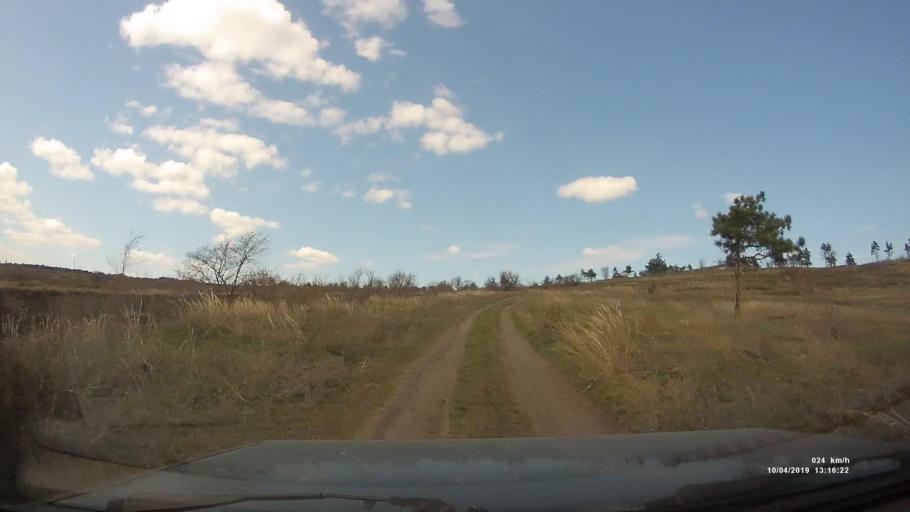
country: RU
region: Rostov
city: Masalovka
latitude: 48.4207
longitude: 40.2563
